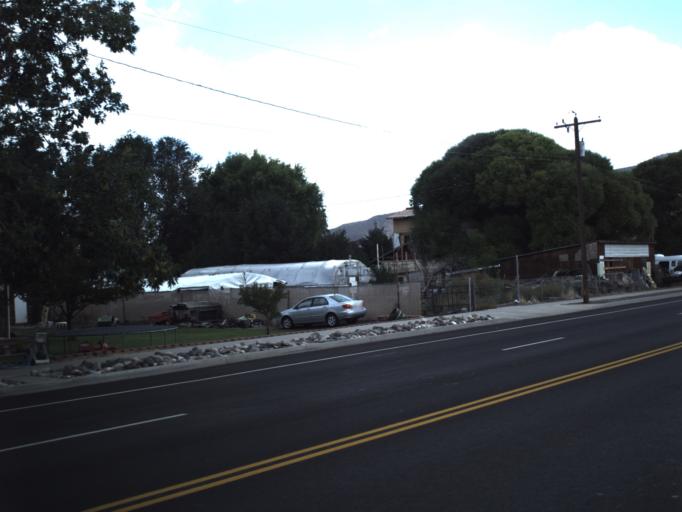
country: US
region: Utah
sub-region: Sevier County
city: Monroe
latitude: 38.6302
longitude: -112.1273
